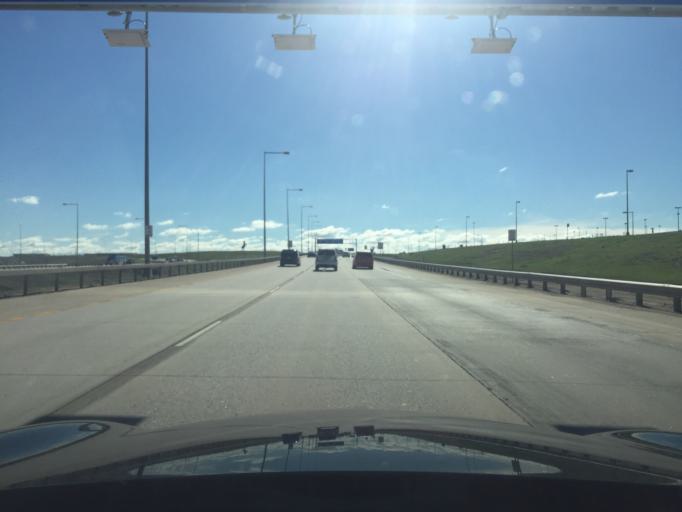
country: US
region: Colorado
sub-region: Weld County
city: Lochbuie
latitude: 39.8335
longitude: -104.6827
